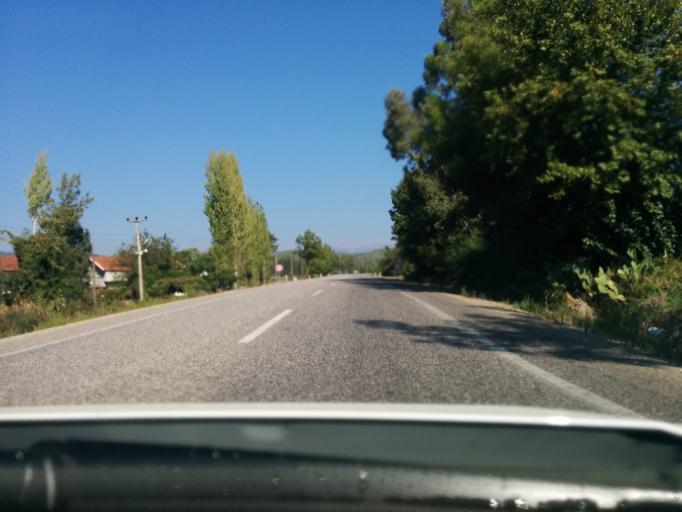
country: TR
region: Mugla
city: Kemer
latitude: 36.5825
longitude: 29.3509
